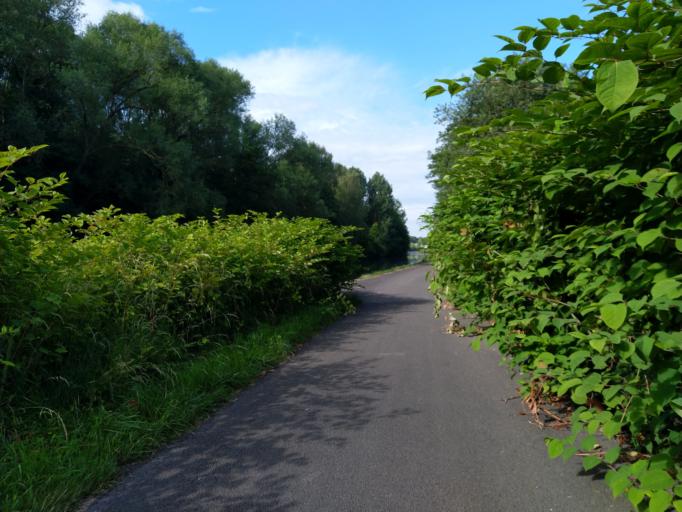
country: BE
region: Wallonia
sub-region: Province du Hainaut
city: Erquelinnes
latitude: 50.3061
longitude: 4.1198
